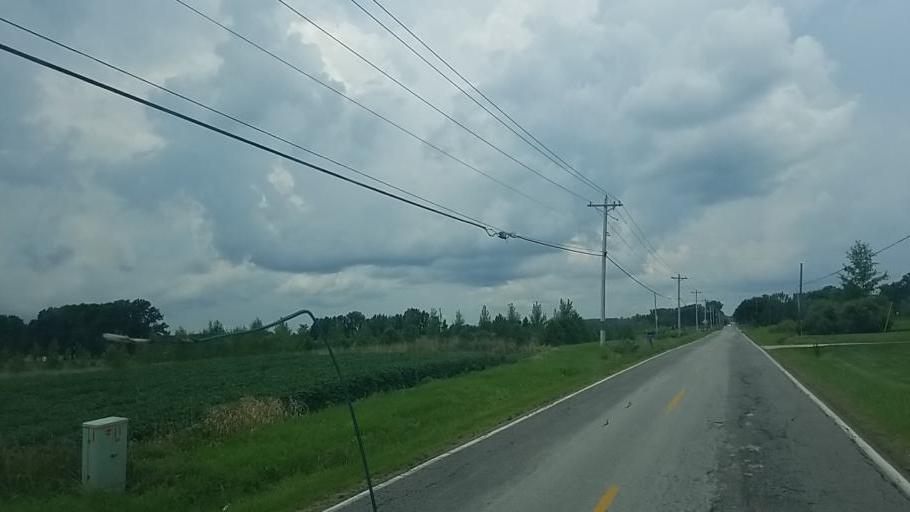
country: US
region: Ohio
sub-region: Lorain County
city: Wellington
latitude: 41.1733
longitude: -82.1691
